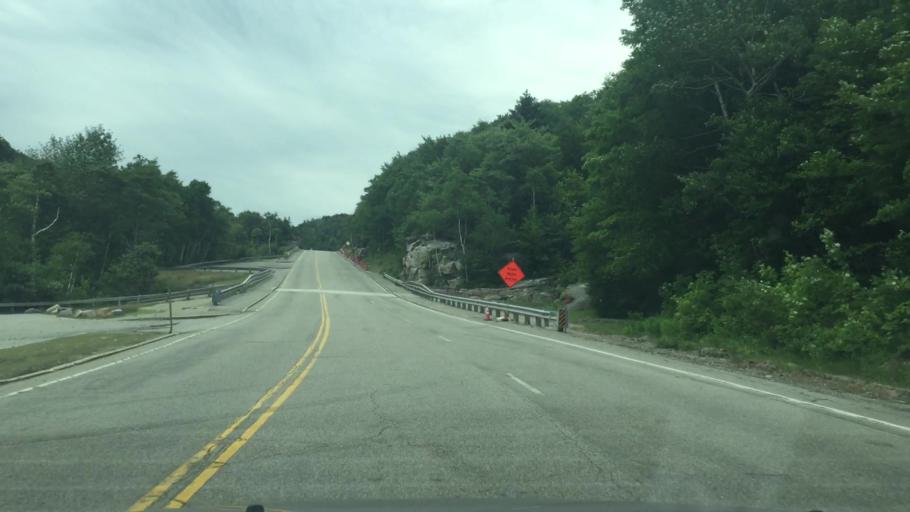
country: US
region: New Hampshire
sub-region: Grafton County
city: Deerfield
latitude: 44.2063
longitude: -71.4030
